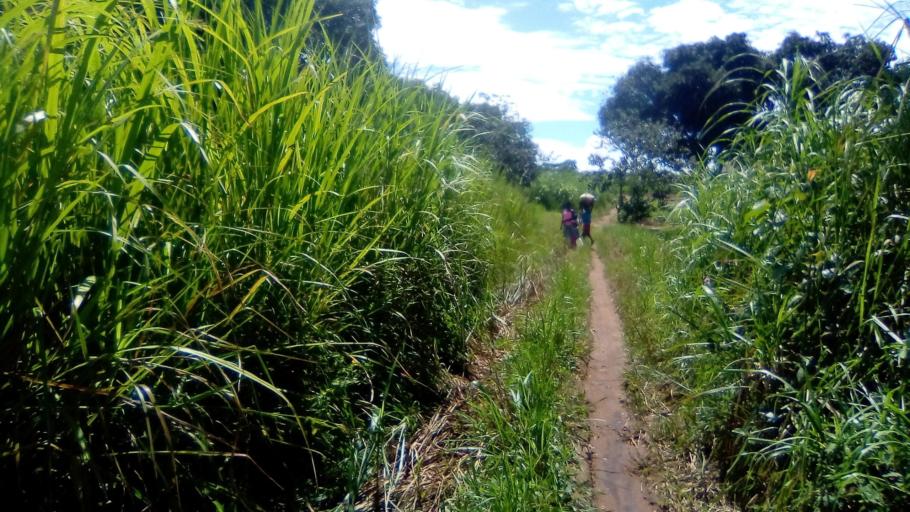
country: SL
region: Eastern Province
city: Simbakoro
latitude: 8.6312
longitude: -11.0010
